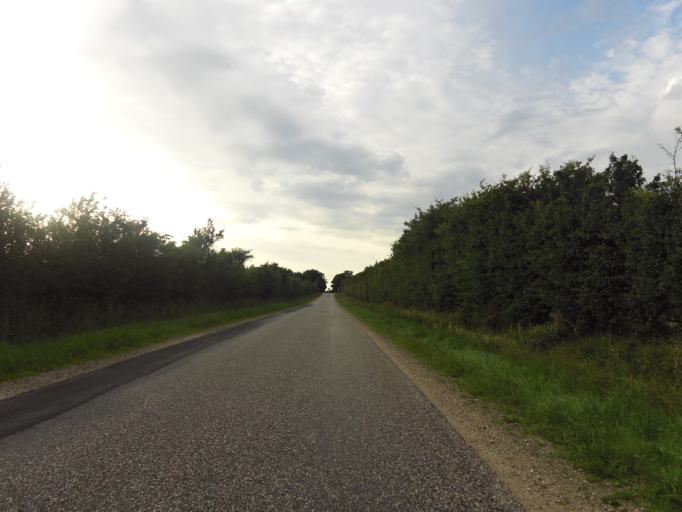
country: DK
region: South Denmark
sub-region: Tonder Kommune
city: Logumkloster
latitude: 55.1774
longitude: 8.9086
